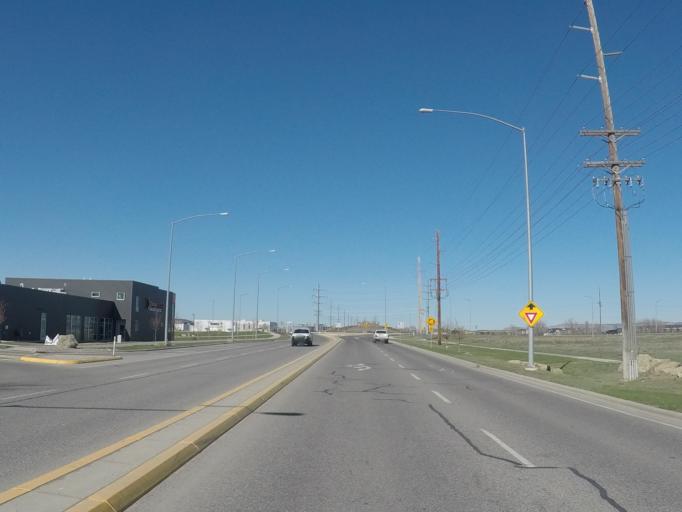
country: US
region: Montana
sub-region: Yellowstone County
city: Billings
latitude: 45.7551
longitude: -108.6150
